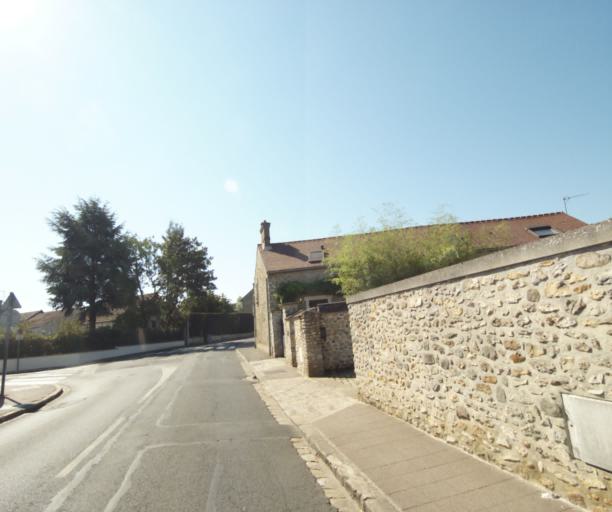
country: FR
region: Ile-de-France
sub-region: Departement de Seine-et-Marne
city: Moissy-Cramayel
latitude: 48.6269
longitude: 2.5951
